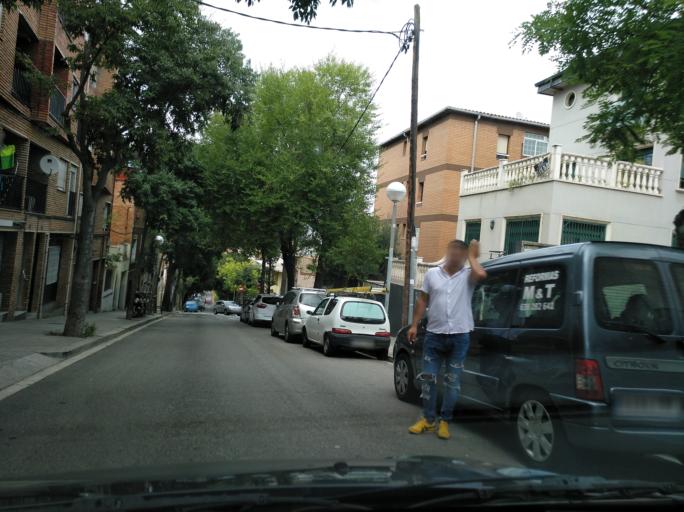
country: ES
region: Catalonia
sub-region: Provincia de Barcelona
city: Horta-Guinardo
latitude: 41.4225
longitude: 2.1583
